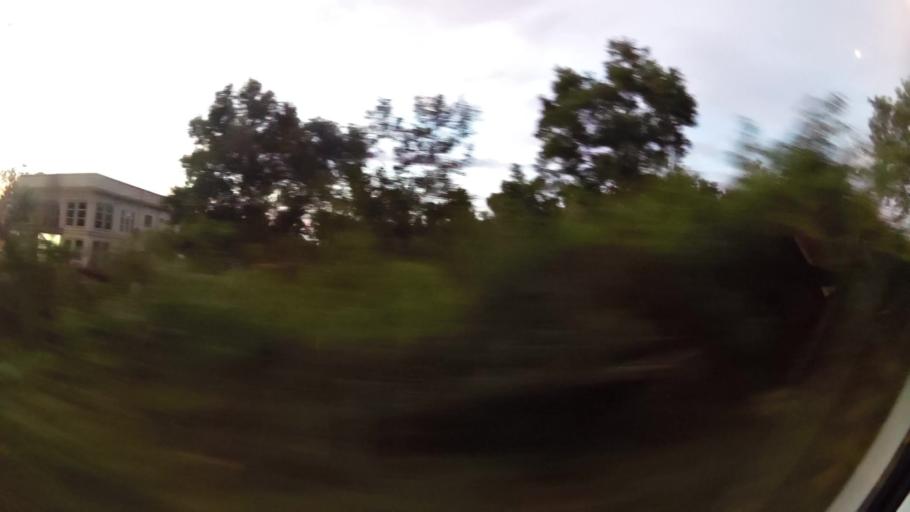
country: BN
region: Belait
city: Seria
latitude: 4.6475
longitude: 114.4119
